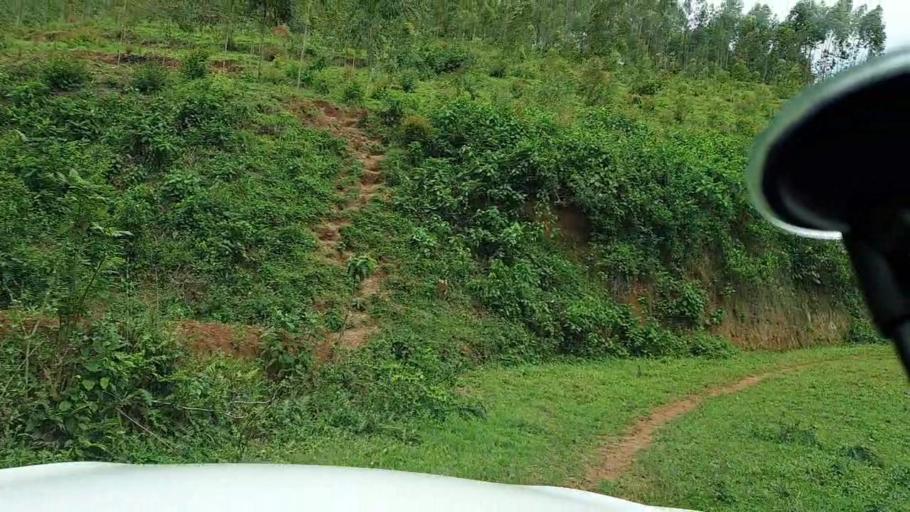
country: RW
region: Southern Province
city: Gitarama
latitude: -2.0813
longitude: 29.6457
